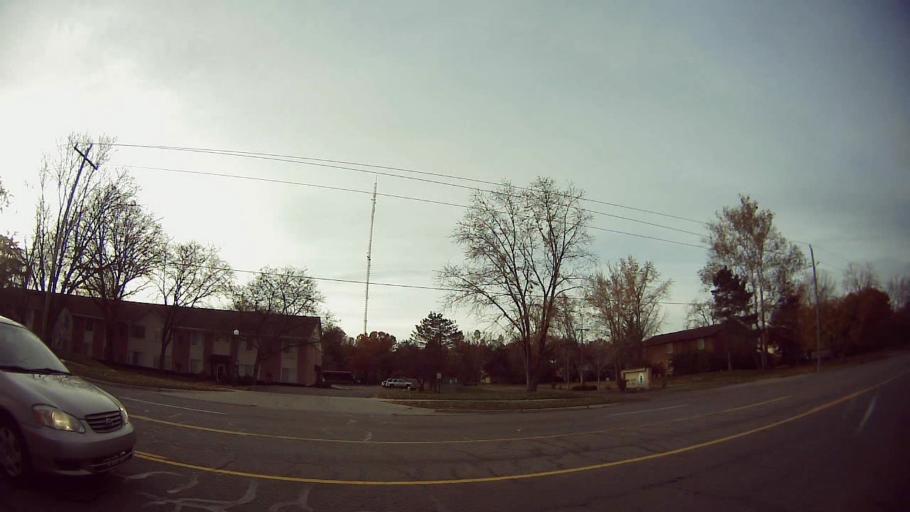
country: US
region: Michigan
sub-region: Oakland County
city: Lathrup Village
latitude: 42.4884
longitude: -83.2040
